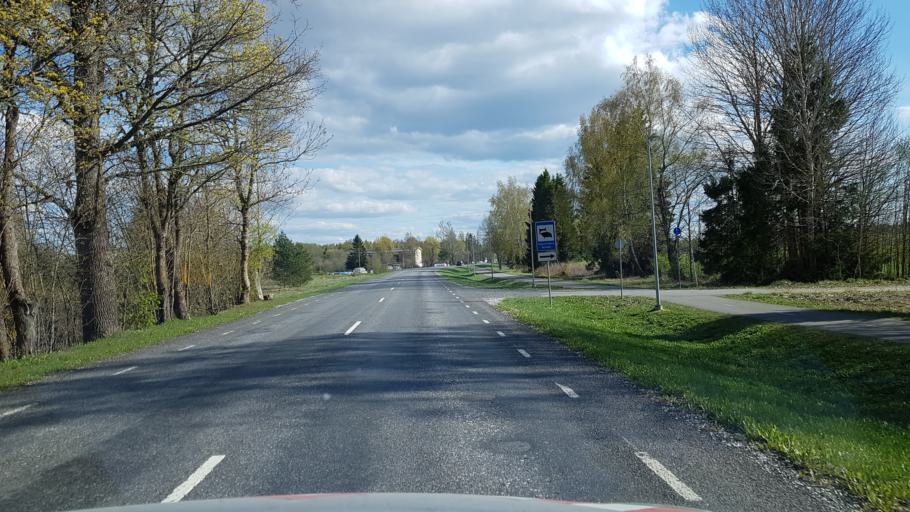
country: EE
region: Raplamaa
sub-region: Kohila vald
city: Kohila
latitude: 59.1408
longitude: 24.7791
